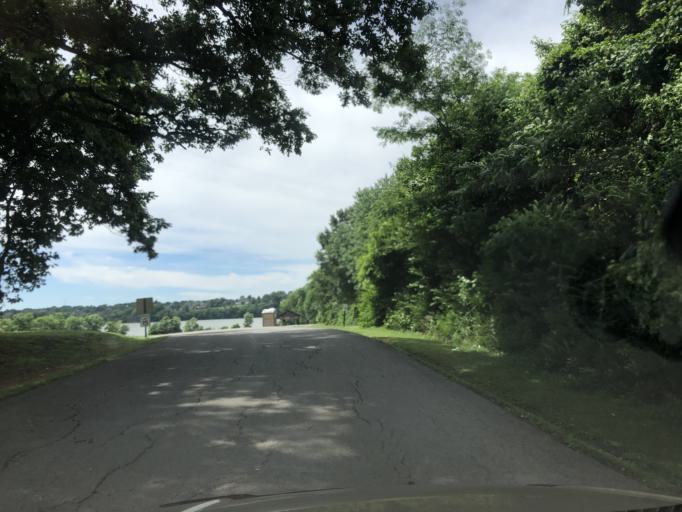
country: US
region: Tennessee
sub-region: Davidson County
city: Lakewood
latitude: 36.2509
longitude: -86.6078
